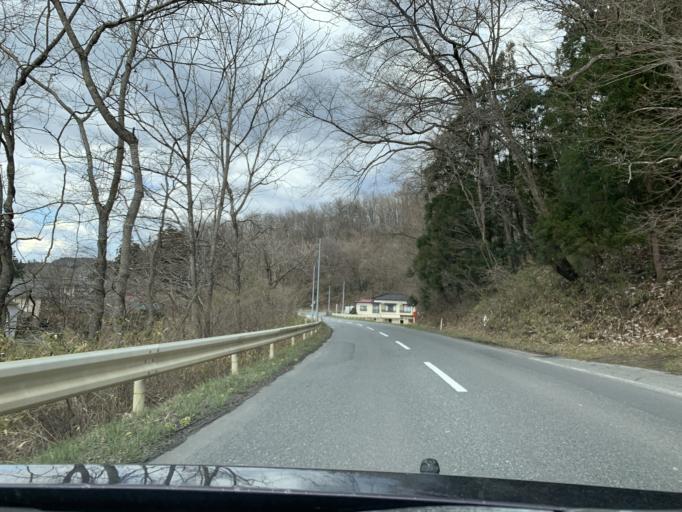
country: JP
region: Iwate
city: Ichinoseki
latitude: 38.8421
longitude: 141.3415
